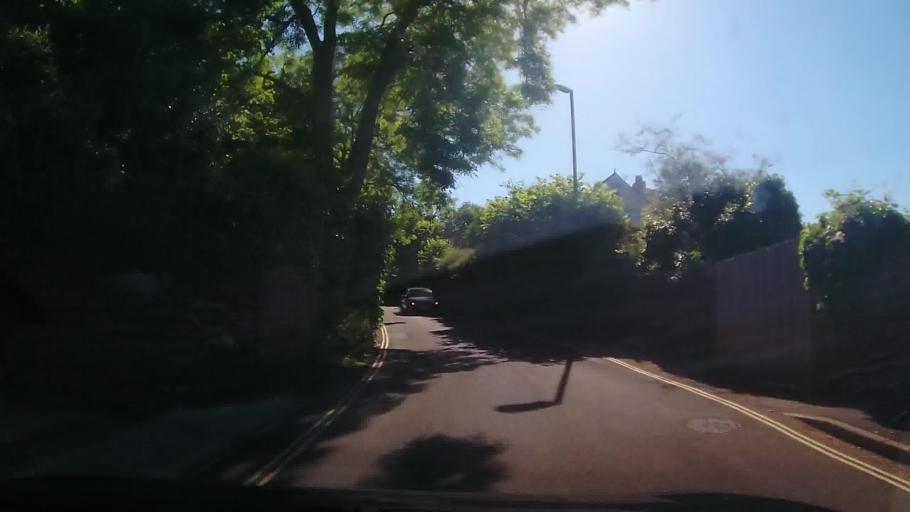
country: GB
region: England
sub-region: Borough of Torbay
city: Brixham
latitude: 50.3806
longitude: -3.5302
